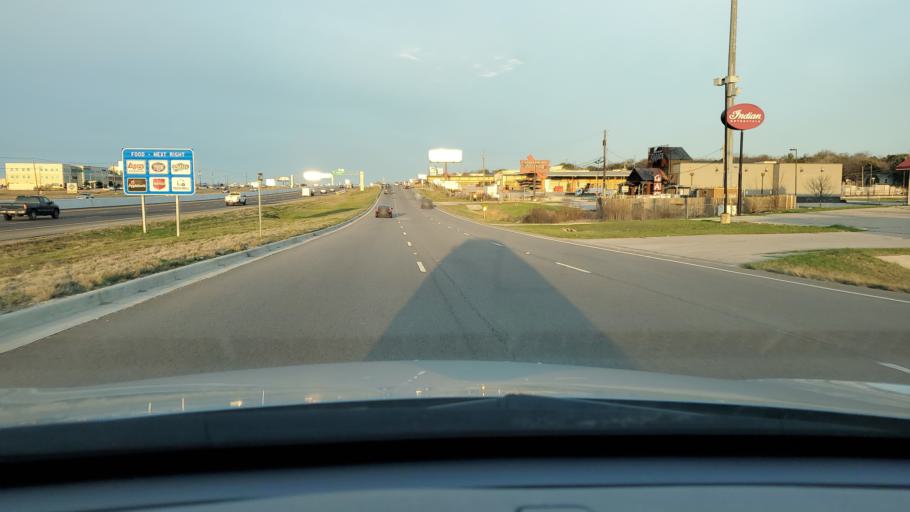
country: US
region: Texas
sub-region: Bell County
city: Harker Heights
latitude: 31.0728
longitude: -97.6763
